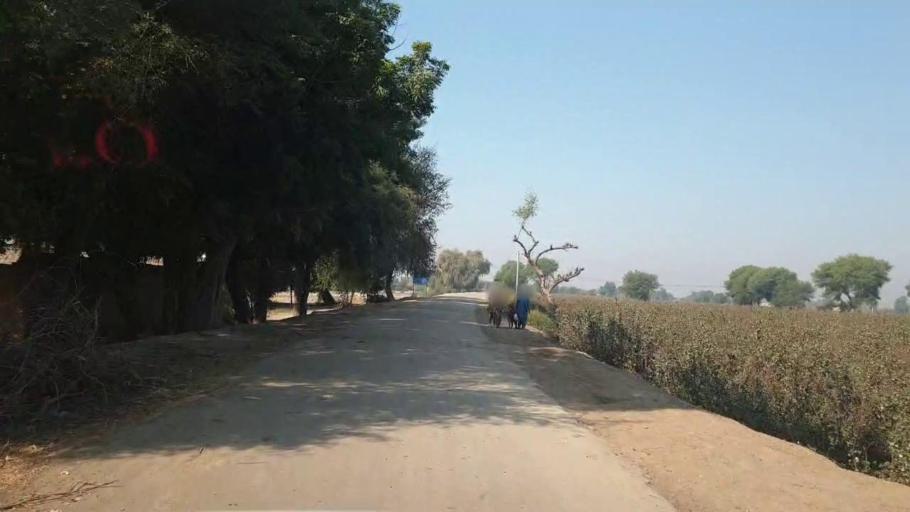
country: PK
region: Sindh
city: Bhan
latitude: 26.6039
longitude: 67.7462
